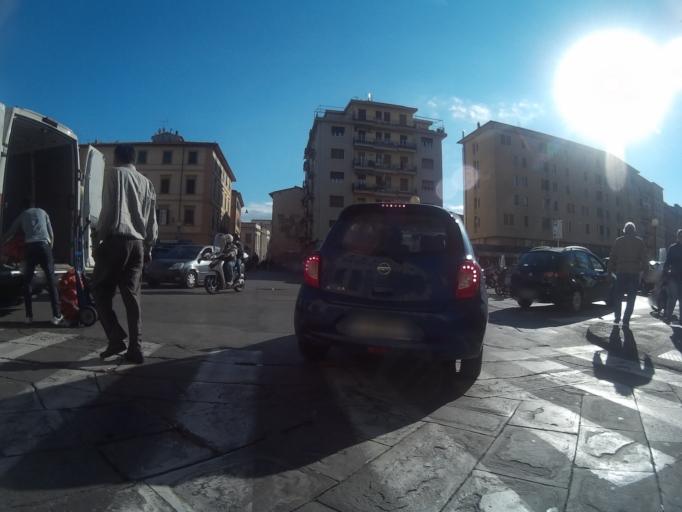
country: IT
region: Tuscany
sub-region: Provincia di Livorno
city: Livorno
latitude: 43.5509
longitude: 10.3137
